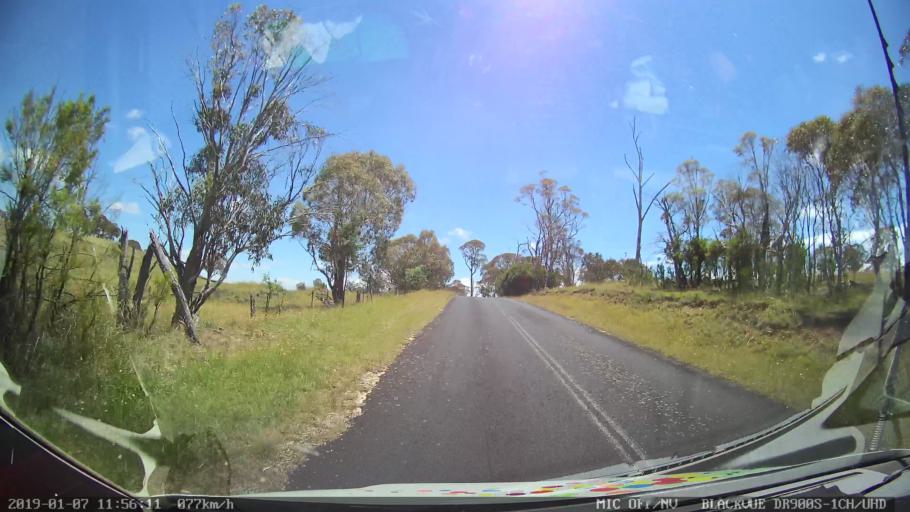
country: AU
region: New South Wales
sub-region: Guyra
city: Guyra
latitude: -30.2775
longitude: 151.6740
